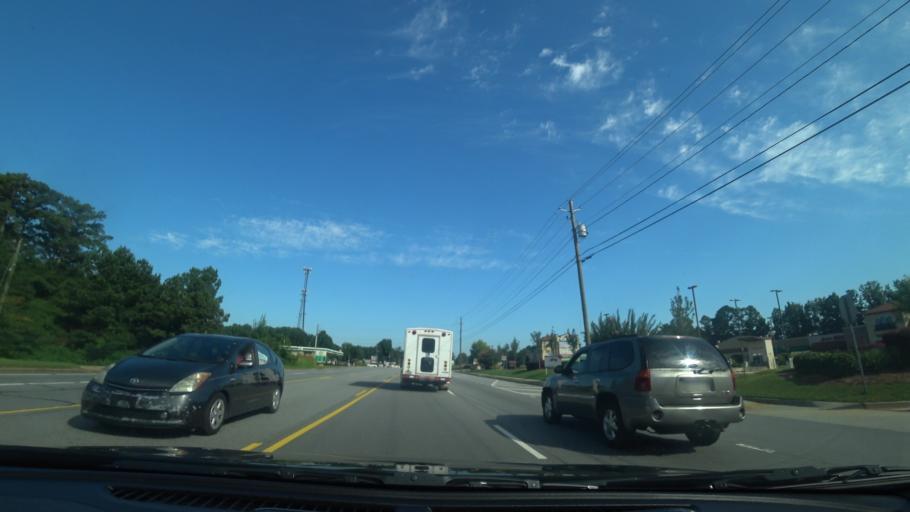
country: US
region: Georgia
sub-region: Gwinnett County
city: Lawrenceville
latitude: 33.9320
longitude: -83.9770
